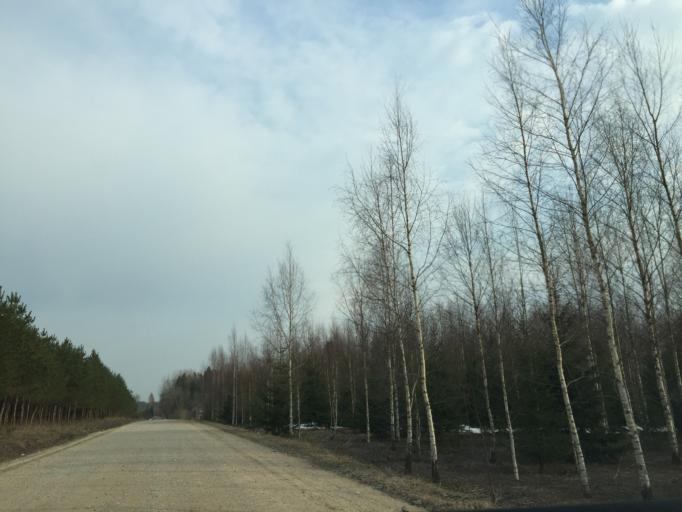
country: LV
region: Raunas
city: Rauna
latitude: 57.1542
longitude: 25.5808
